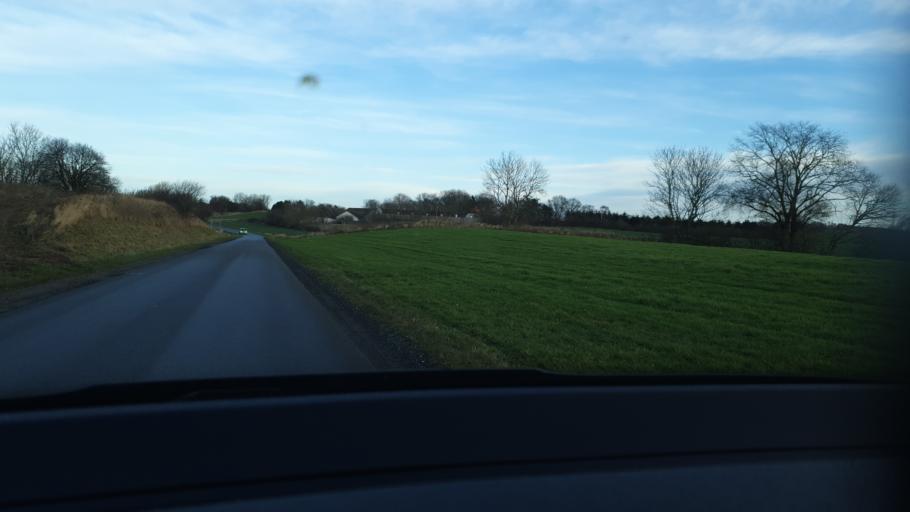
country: DK
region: Zealand
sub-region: Odsherred Kommune
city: Hojby
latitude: 55.9149
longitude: 11.6131
